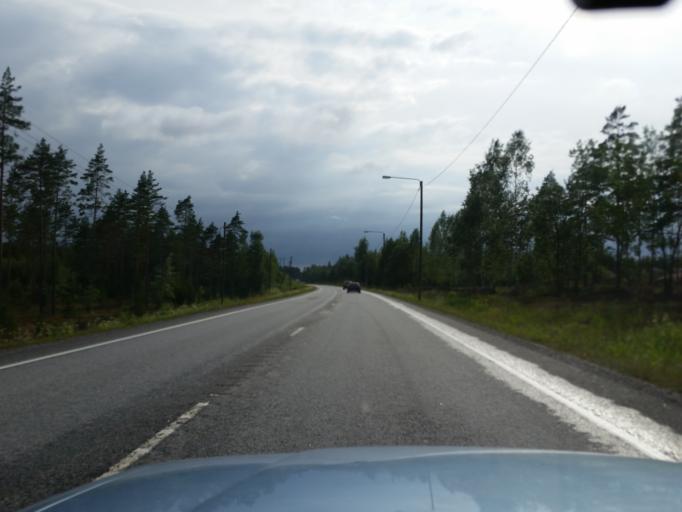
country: FI
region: Uusimaa
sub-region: Raaseporin
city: Pohja
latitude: 60.0146
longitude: 23.5577
